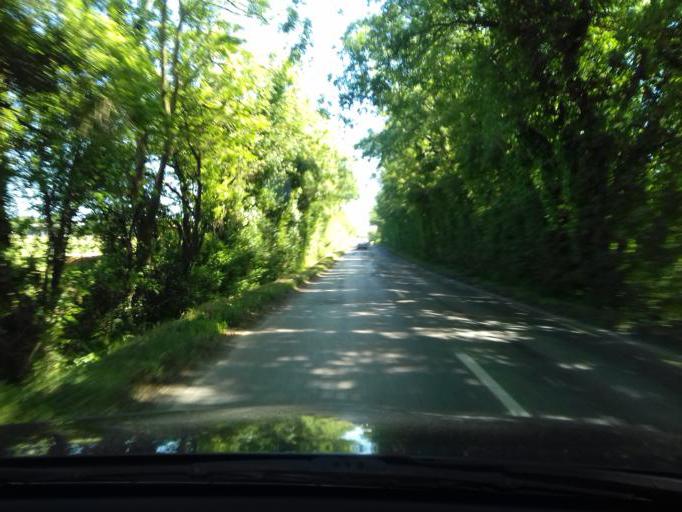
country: IE
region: Leinster
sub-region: An Mhi
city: Stamullin
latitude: 53.5641
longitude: -6.2763
